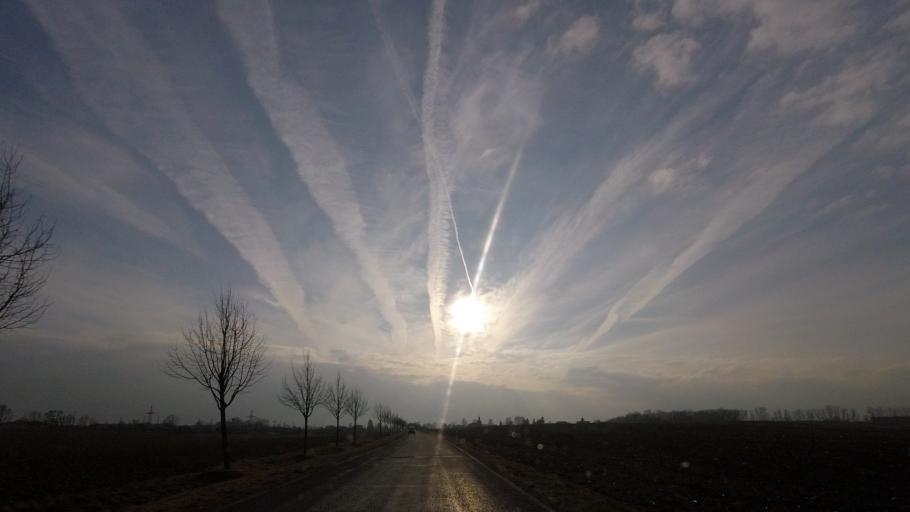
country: DE
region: Brandenburg
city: Belzig
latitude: 52.1157
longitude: 12.5445
